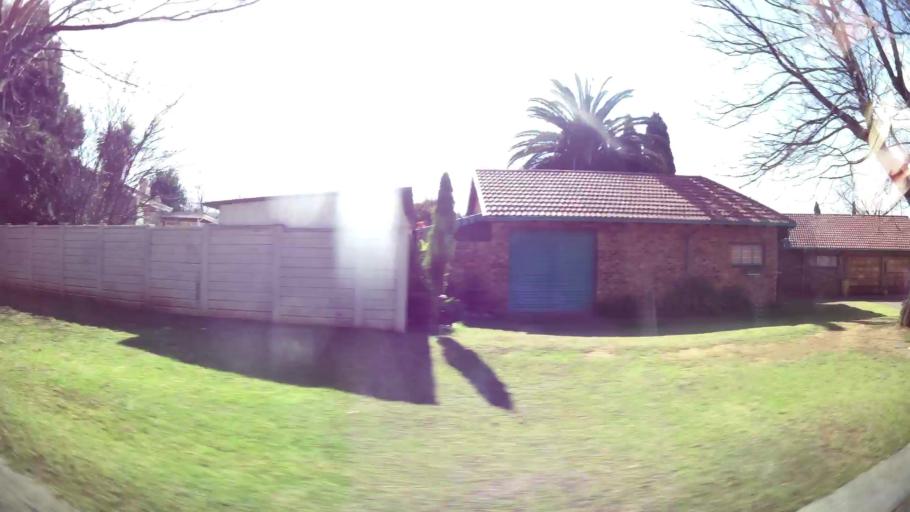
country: ZA
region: Gauteng
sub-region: Ekurhuleni Metropolitan Municipality
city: Benoni
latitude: -26.1409
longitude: 28.3505
